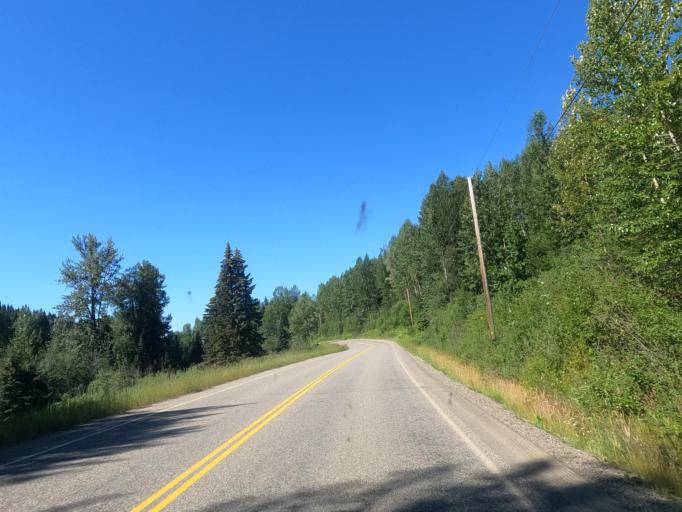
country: CA
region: British Columbia
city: Quesnel
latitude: 53.0437
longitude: -121.9705
